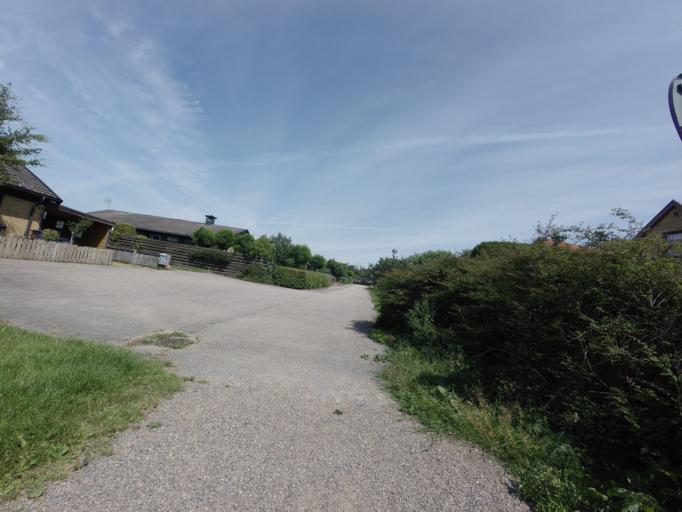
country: SE
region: Skane
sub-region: Helsingborg
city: Glumslov
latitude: 55.9427
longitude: 12.8062
